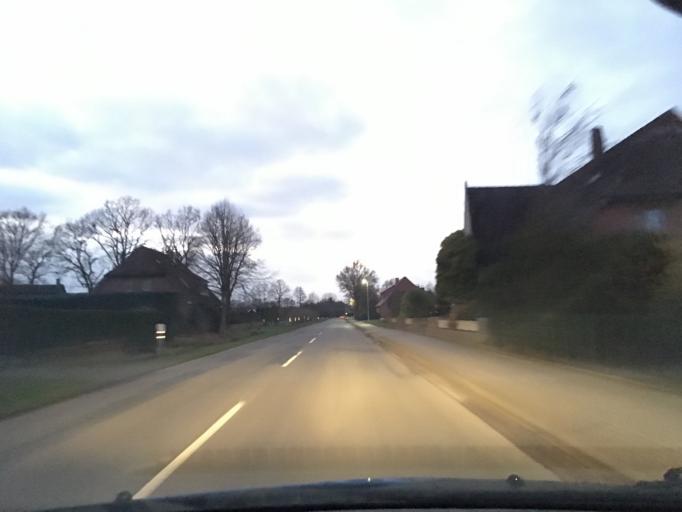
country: DE
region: Lower Saxony
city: Brietlingen
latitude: 53.3278
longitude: 10.4571
